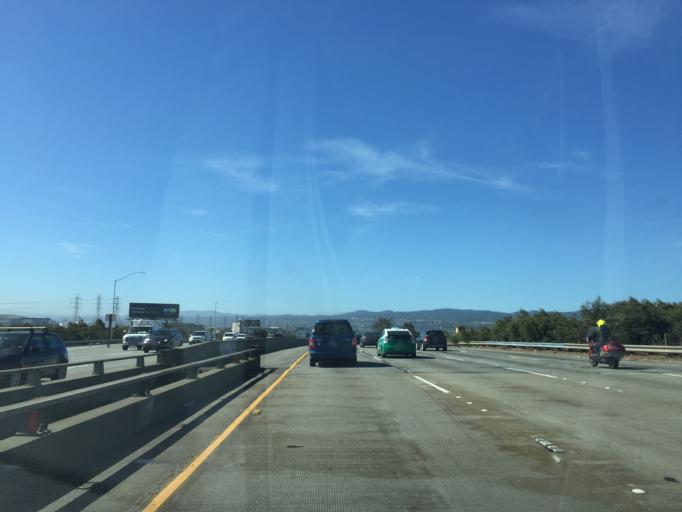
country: US
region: California
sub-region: San Mateo County
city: South San Francisco
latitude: 37.6532
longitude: -122.4071
